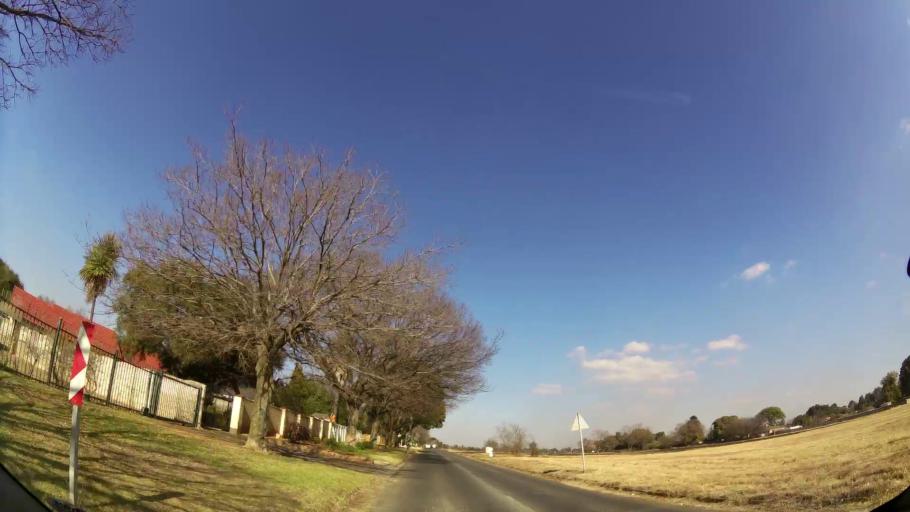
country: ZA
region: Gauteng
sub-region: Ekurhuleni Metropolitan Municipality
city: Benoni
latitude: -26.1437
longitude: 28.3353
